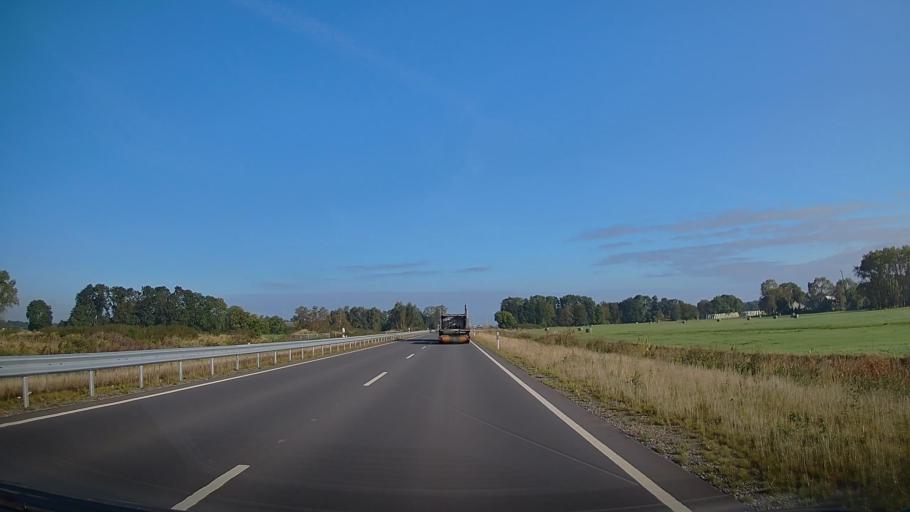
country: DE
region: Lower Saxony
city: Ovelgonne
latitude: 53.3050
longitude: 8.3973
